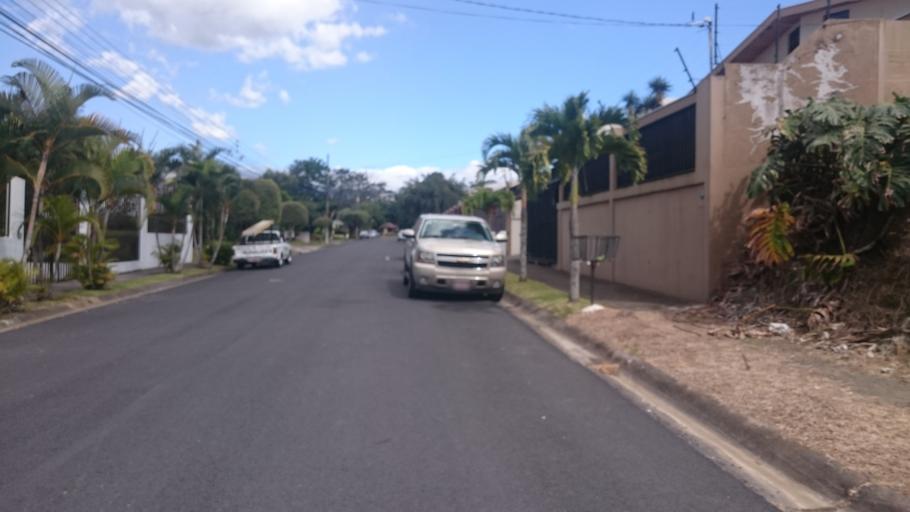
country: CR
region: San Jose
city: Curridabat
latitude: 9.9262
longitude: -84.0298
